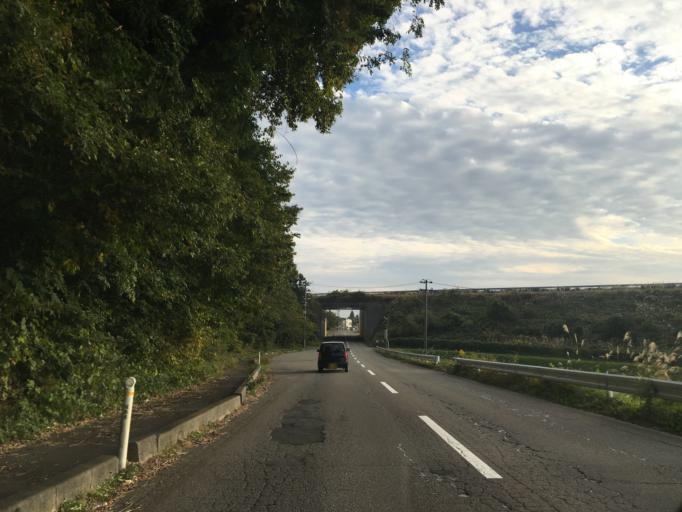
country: JP
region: Fukushima
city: Inawashiro
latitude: 37.5283
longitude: 140.1449
